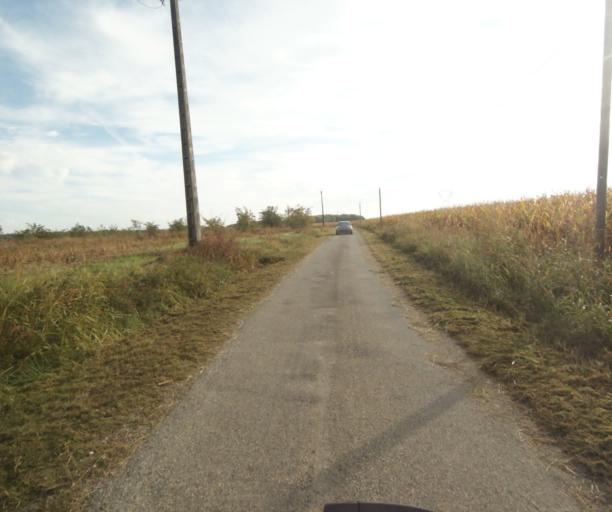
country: FR
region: Midi-Pyrenees
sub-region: Departement du Tarn-et-Garonne
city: Montech
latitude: 43.9788
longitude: 1.2247
